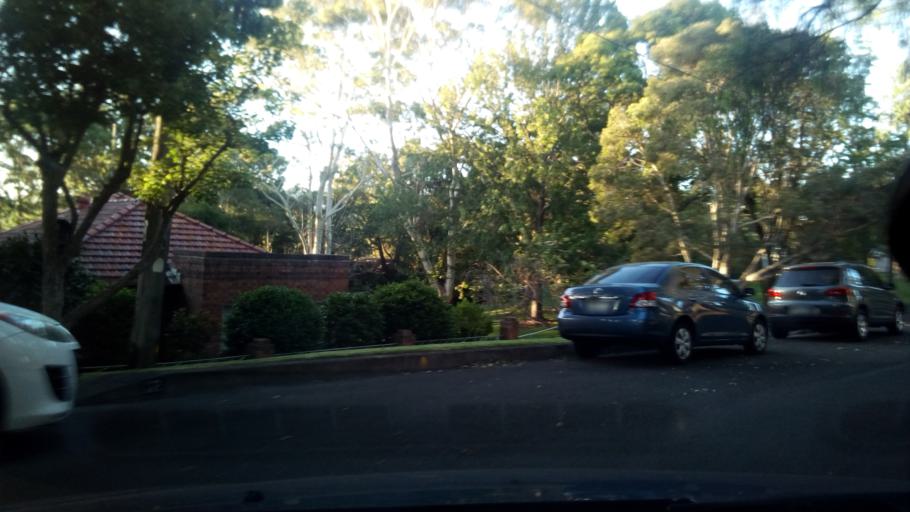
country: AU
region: New South Wales
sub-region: Wollongong
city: Mangerton
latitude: -34.4332
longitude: 150.8773
